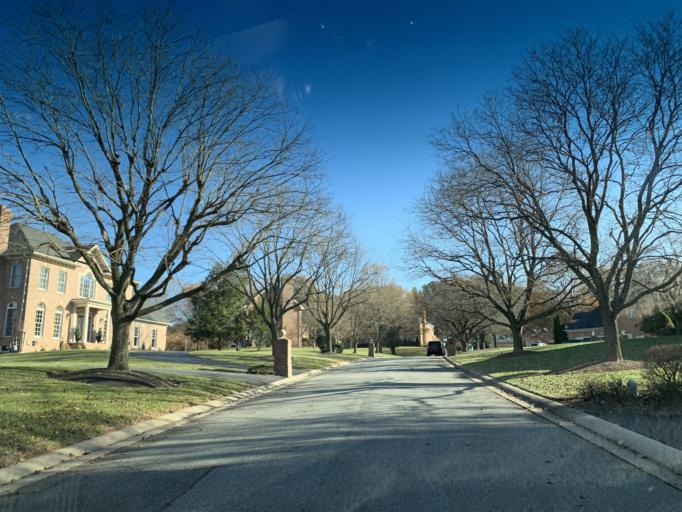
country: US
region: Maryland
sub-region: Harford County
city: Bel Air South
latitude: 39.5184
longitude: -76.3055
